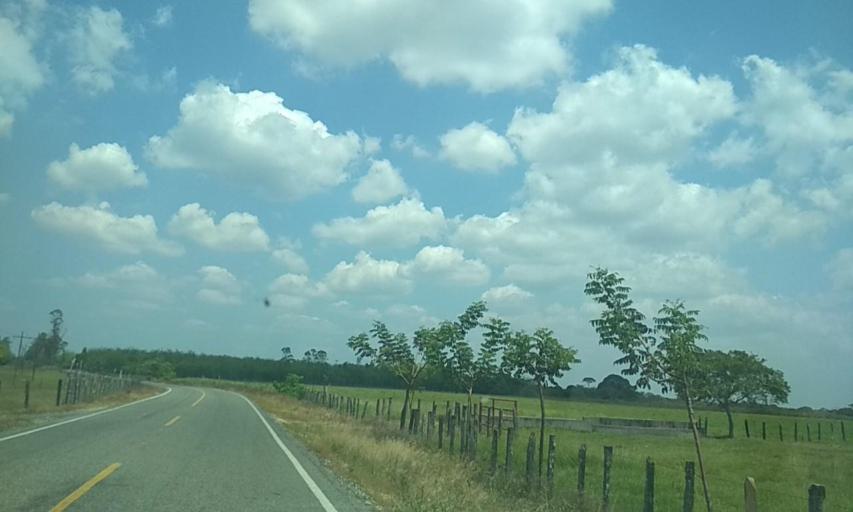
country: MX
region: Tabasco
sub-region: Huimanguillo
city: Huapacal 1ra. Seccion
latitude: 17.7520
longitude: -93.7150
